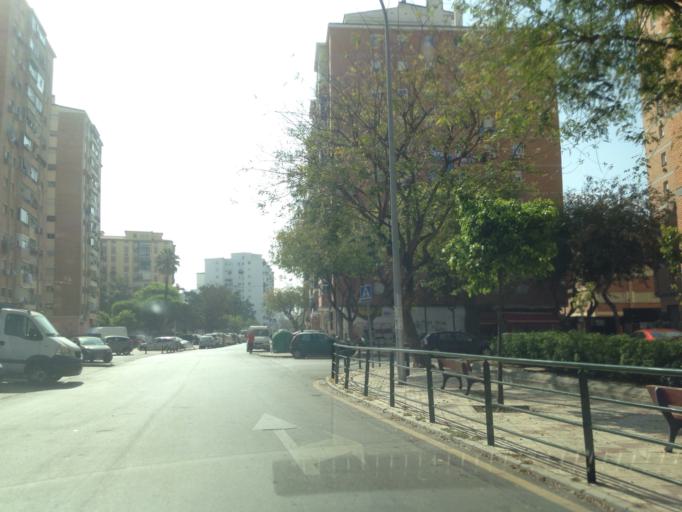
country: ES
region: Andalusia
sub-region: Provincia de Malaga
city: Malaga
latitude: 36.6995
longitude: -4.4531
